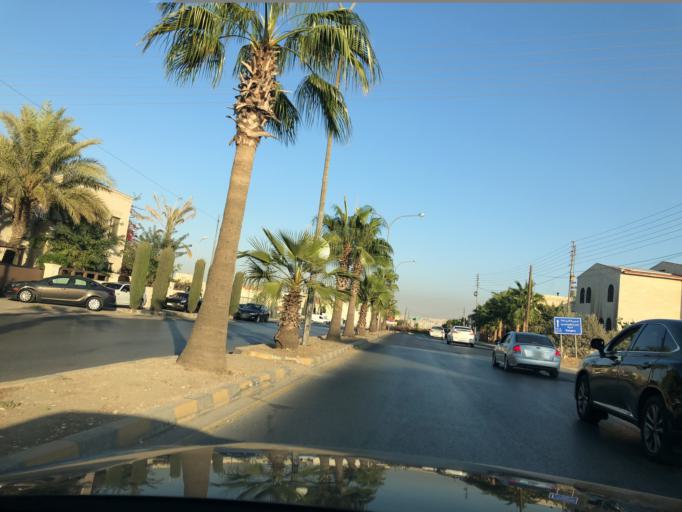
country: JO
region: Amman
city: Al Bunayyat ash Shamaliyah
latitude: 31.9428
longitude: 35.8792
